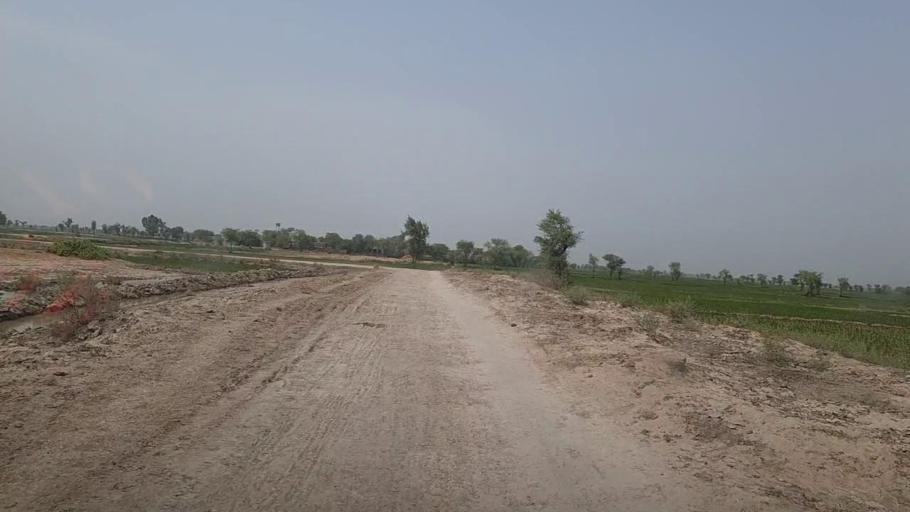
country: PK
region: Sindh
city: Sita Road
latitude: 27.0924
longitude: 67.8556
